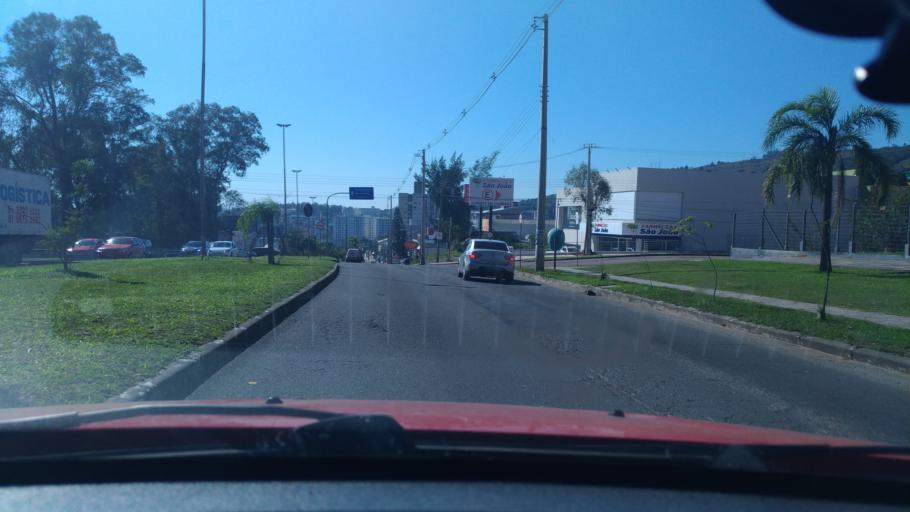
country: BR
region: Rio Grande do Sul
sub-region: Porto Alegre
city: Porto Alegre
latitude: -30.0431
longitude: -51.1377
